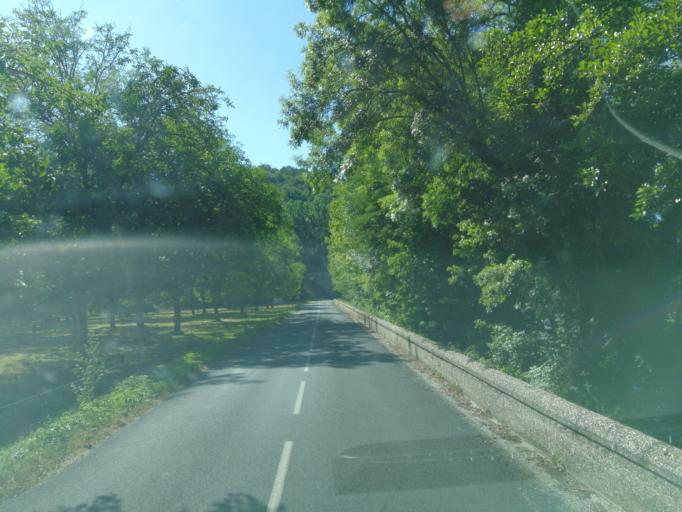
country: FR
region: Midi-Pyrenees
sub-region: Departement du Lot
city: Souillac
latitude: 44.8712
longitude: 1.4139
